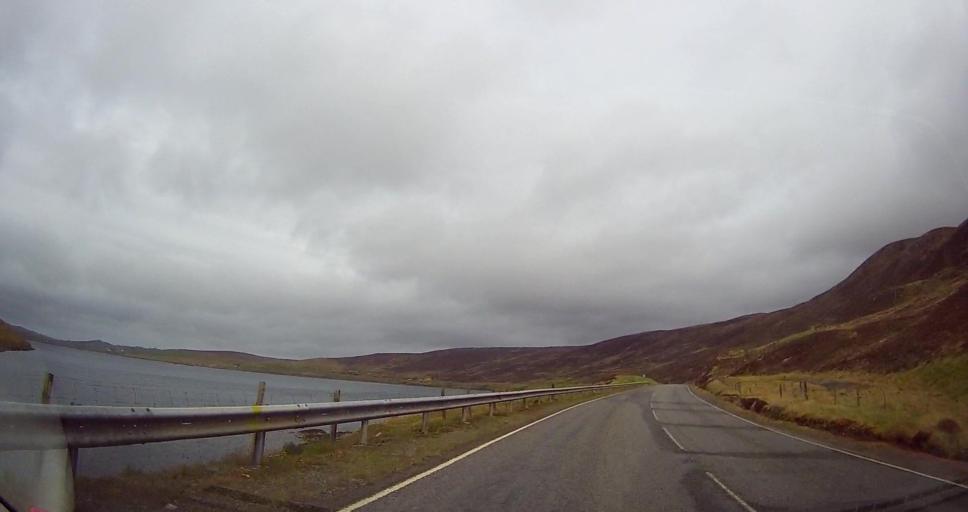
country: GB
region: Scotland
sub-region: Shetland Islands
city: Lerwick
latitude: 60.3574
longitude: -1.2848
